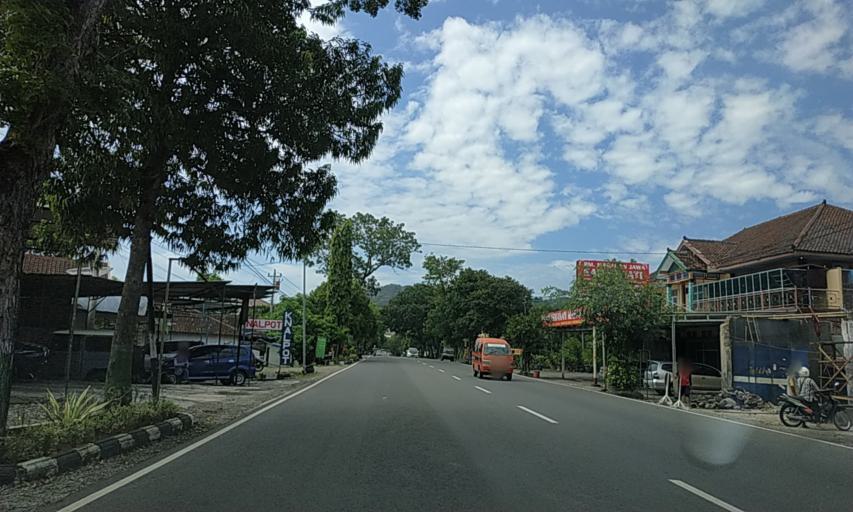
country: ID
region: Central Java
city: Selogiri
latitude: -7.8009
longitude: 110.9104
